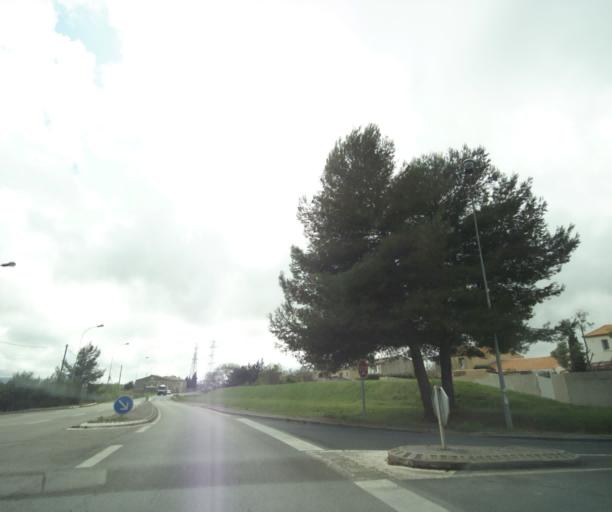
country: FR
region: Languedoc-Roussillon
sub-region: Departement de l'Herault
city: Fabregues
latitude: 43.5451
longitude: 3.7742
